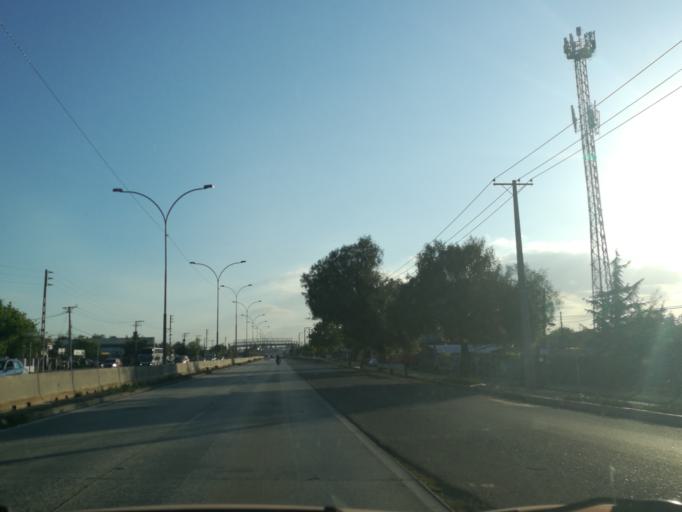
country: CL
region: O'Higgins
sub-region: Provincia de Cachapoal
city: Rancagua
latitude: -34.1802
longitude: -70.7348
